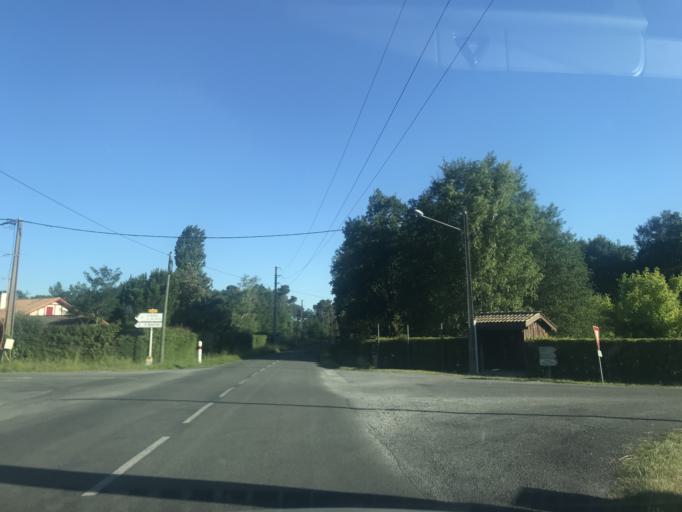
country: FR
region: Aquitaine
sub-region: Departement de la Gironde
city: Saint-Savin
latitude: 45.1136
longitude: -0.4613
